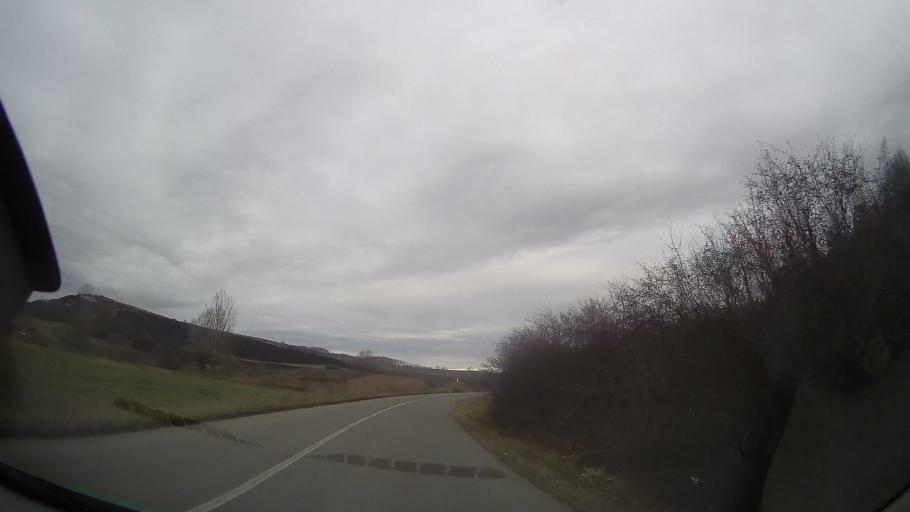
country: RO
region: Mures
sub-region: Comuna Bala
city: Bala
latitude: 46.7270
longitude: 24.5433
